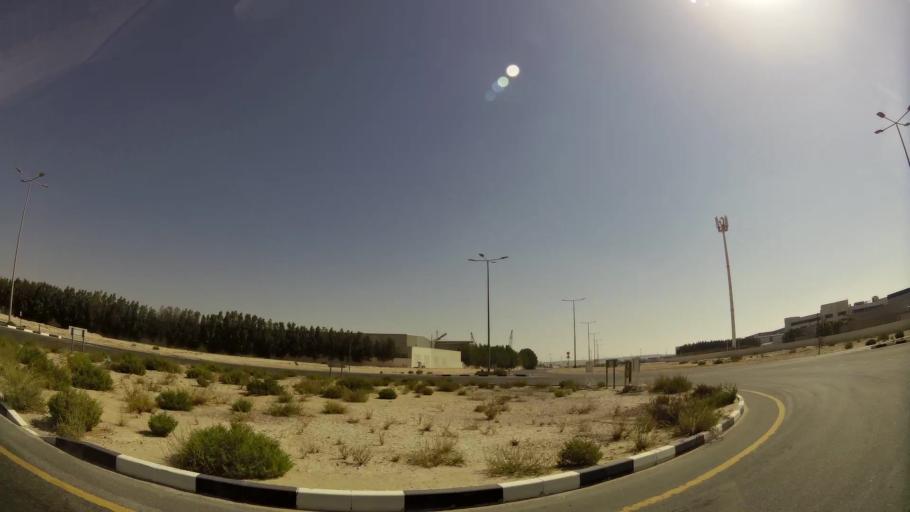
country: AE
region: Dubai
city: Dubai
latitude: 24.9172
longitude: 55.0647
